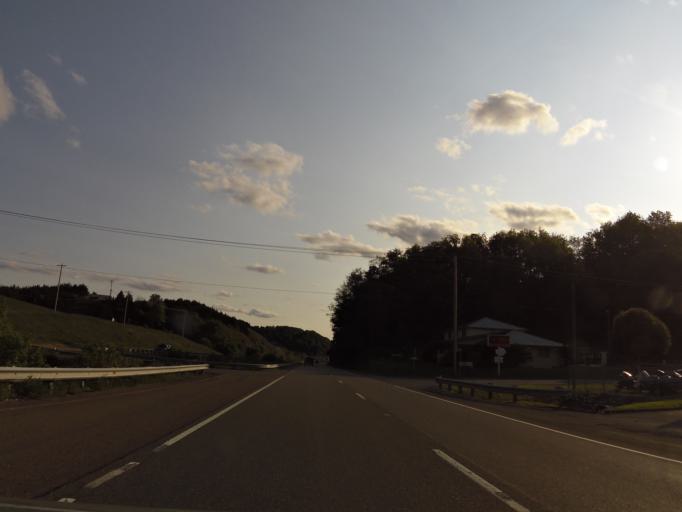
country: US
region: Virginia
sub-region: Tazewell County
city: Claypool Hill
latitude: 37.0477
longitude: -81.7802
